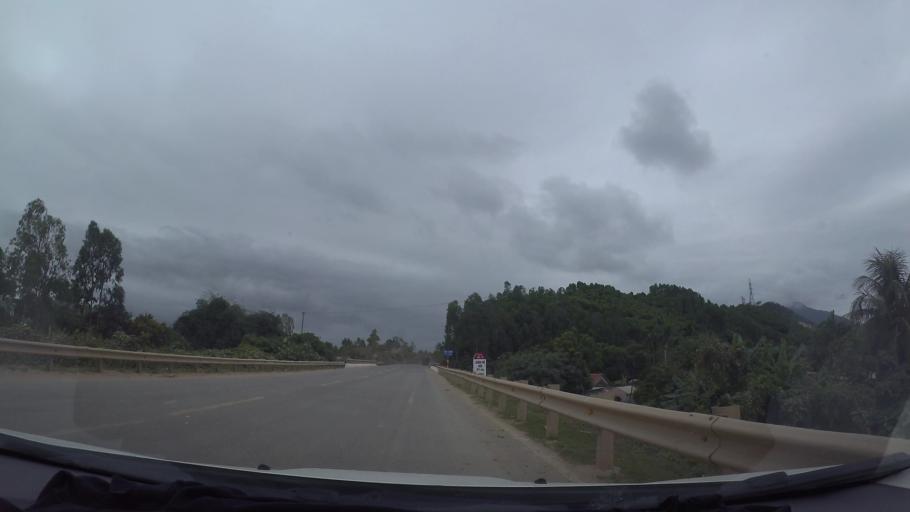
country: VN
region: Da Nang
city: Lien Chieu
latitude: 16.1027
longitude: 108.0982
